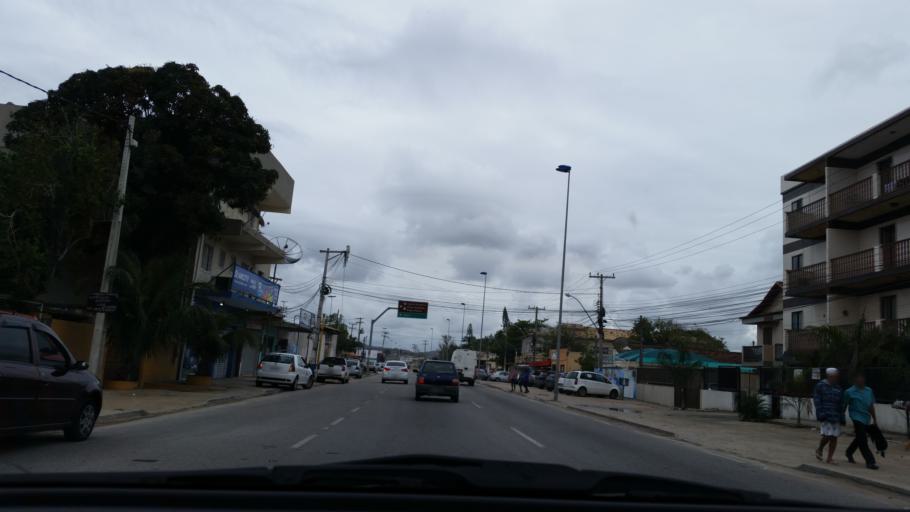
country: BR
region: Rio de Janeiro
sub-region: Sao Pedro Da Aldeia
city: Sao Pedro da Aldeia
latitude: -22.8325
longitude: -42.1047
